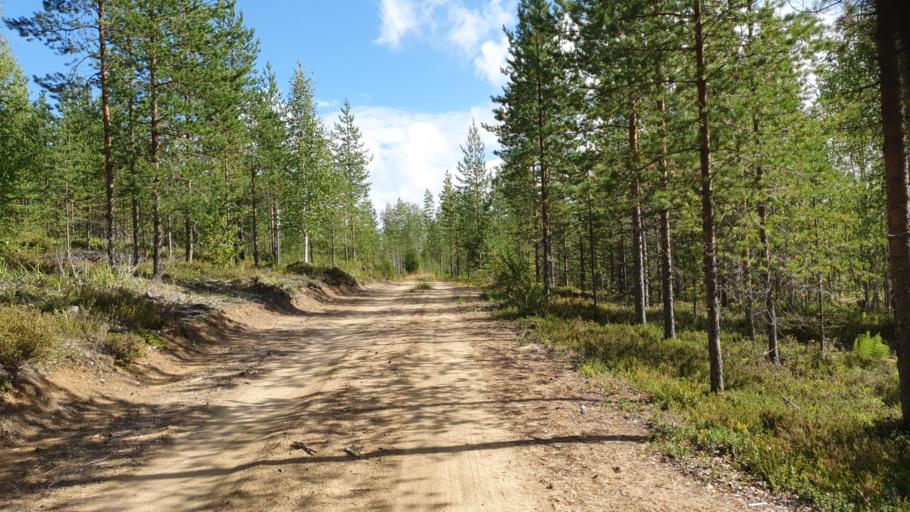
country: FI
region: Kainuu
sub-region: Kehys-Kainuu
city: Kuhmo
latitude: 64.1484
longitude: 29.3629
